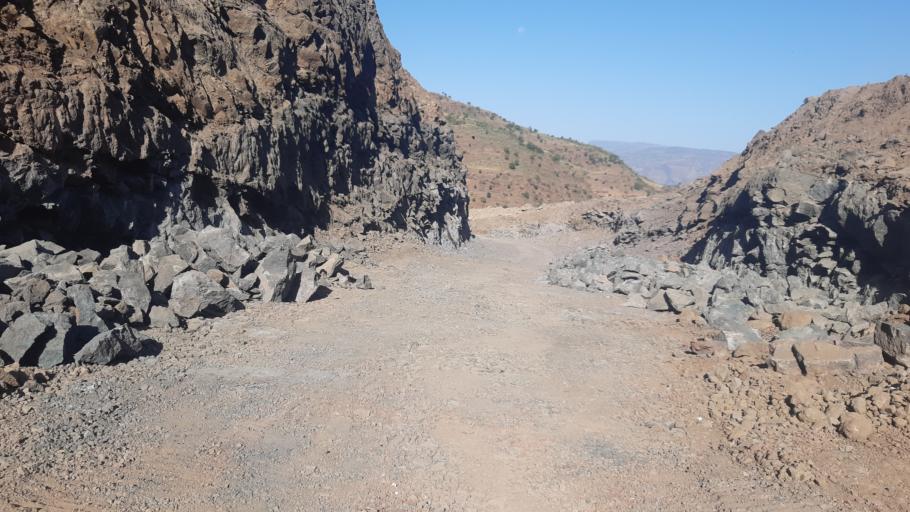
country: ET
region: Amhara
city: Dabat
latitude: 13.1670
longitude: 37.6046
